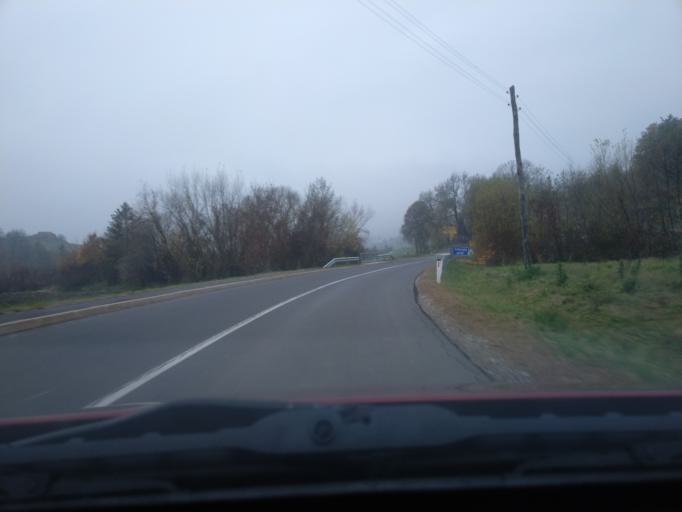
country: SI
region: Kungota
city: Zgornja Kungota
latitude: 46.6483
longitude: 15.6145
